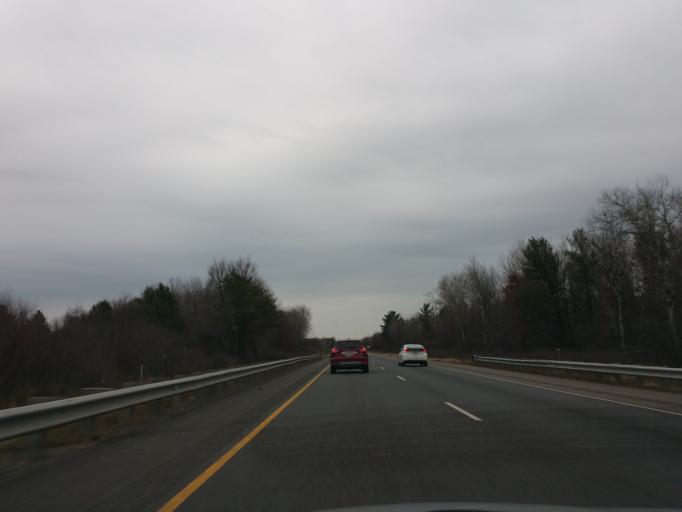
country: US
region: Wisconsin
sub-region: Jackson County
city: Black River Falls
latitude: 44.2607
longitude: -90.7699
